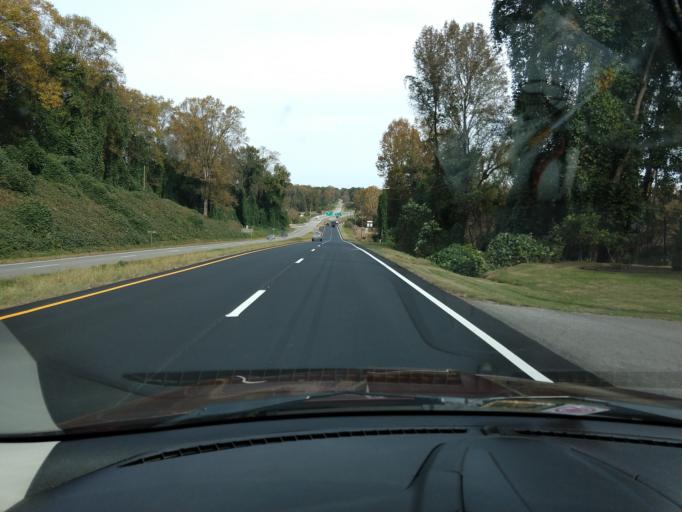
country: US
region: Virginia
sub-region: Pittsylvania County
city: Chatham
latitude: 36.7999
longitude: -79.3934
